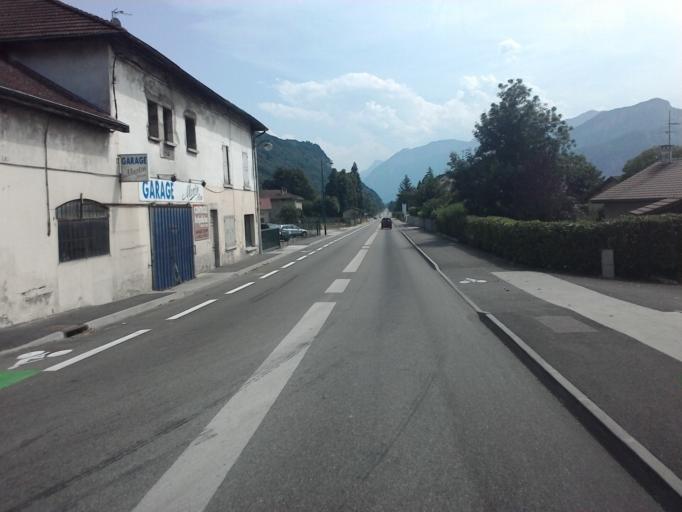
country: FR
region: Rhone-Alpes
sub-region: Departement de l'Isere
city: La Buisse
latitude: 45.3329
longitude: 5.6208
